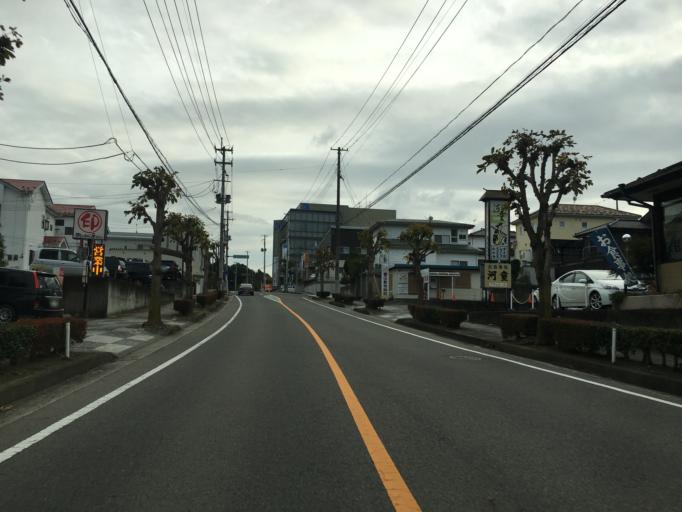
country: JP
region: Fukushima
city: Nihommatsu
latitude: 37.5856
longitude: 140.4325
